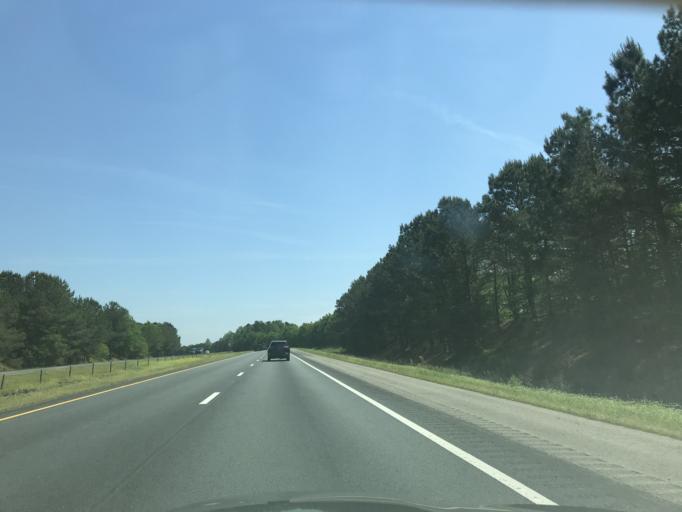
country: US
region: North Carolina
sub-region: Johnston County
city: Benson
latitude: 35.3744
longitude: -78.5030
